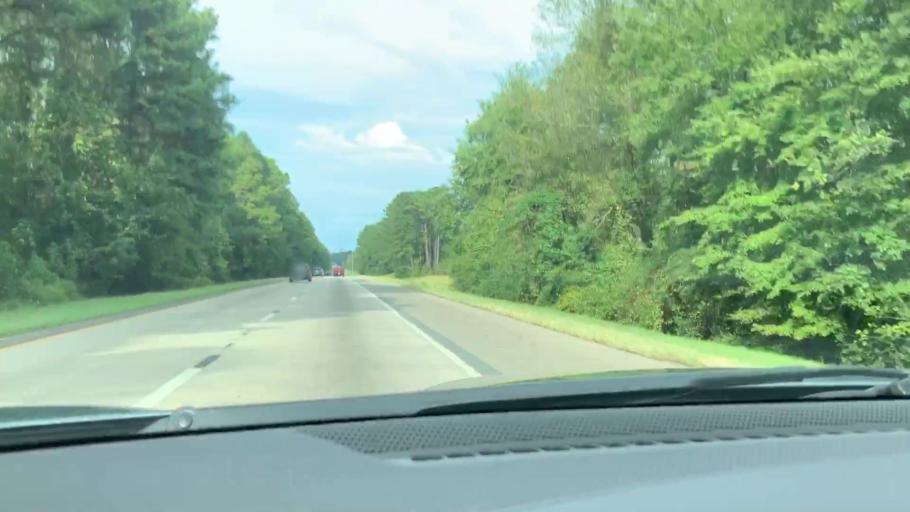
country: US
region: South Carolina
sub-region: Colleton County
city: Walterboro
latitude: 32.8966
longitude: -80.7083
